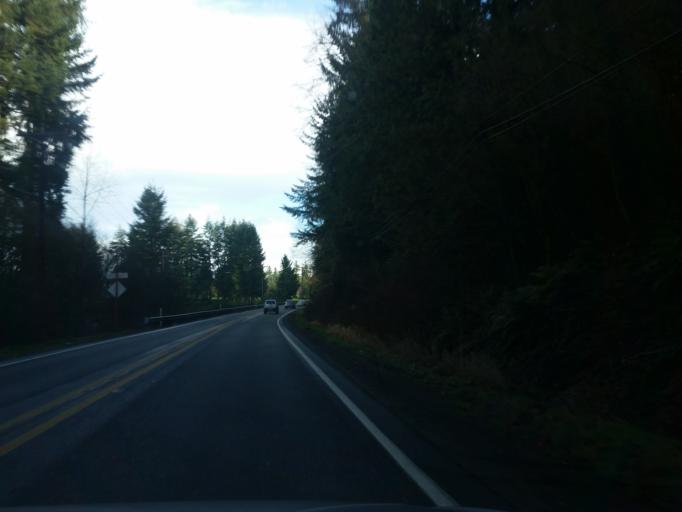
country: US
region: Washington
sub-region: Snohomish County
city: Martha Lake
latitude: 47.8259
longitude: -122.2466
